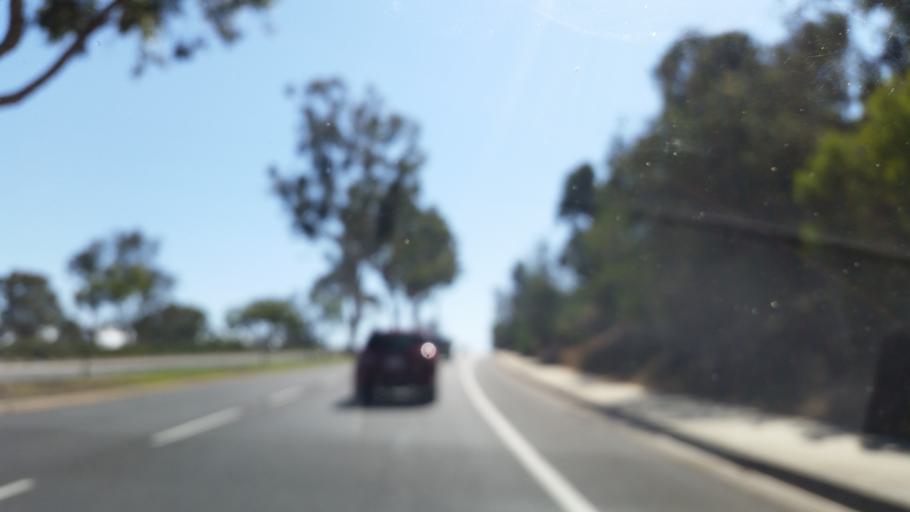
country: US
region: California
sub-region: Orange County
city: Dana Point
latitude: 33.4912
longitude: -117.7205
